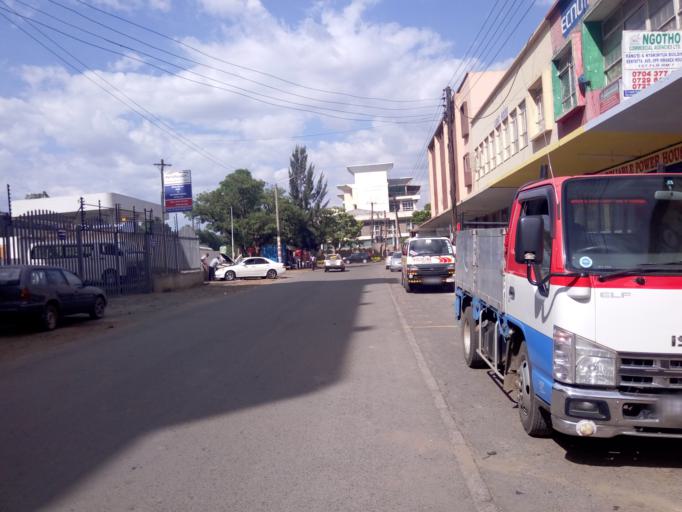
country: KE
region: Nakuru
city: Nakuru
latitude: -0.2846
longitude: 36.0684
